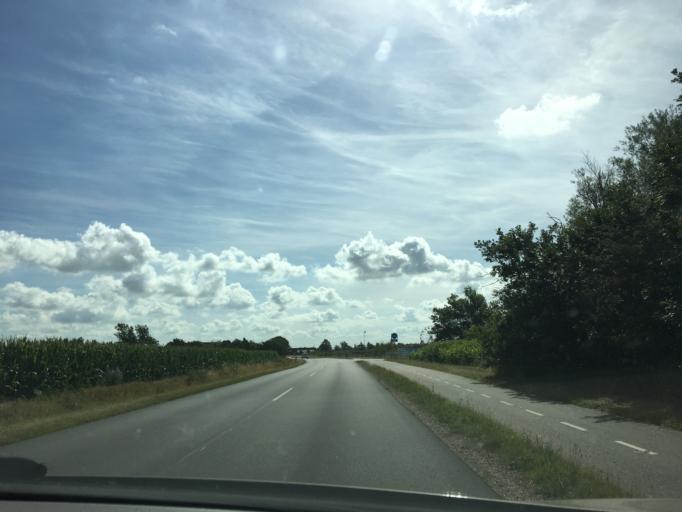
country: DK
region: South Denmark
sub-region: Varde Kommune
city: Oksbol
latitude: 55.8464
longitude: 8.2895
